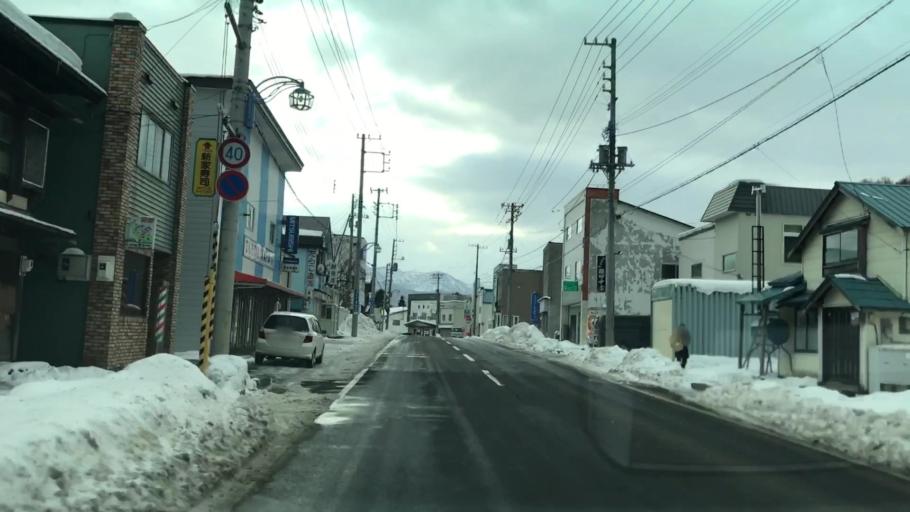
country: JP
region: Hokkaido
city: Yoichi
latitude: 43.2797
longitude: 140.6377
